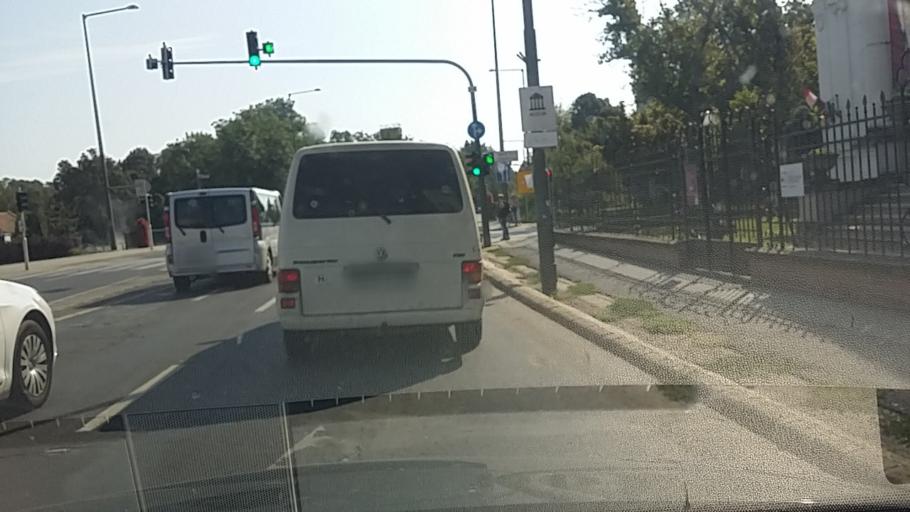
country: HU
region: Bekes
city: Bekescsaba
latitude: 46.6820
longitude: 21.0998
